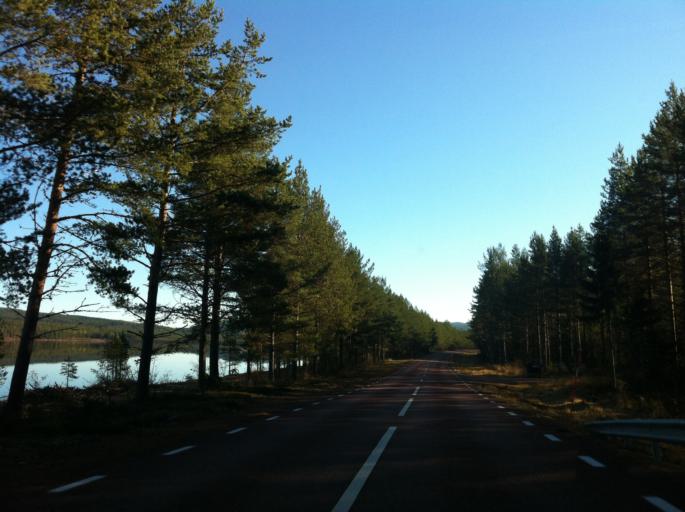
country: SE
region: Dalarna
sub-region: Alvdalens Kommun
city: AElvdalen
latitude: 61.3068
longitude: 13.7212
